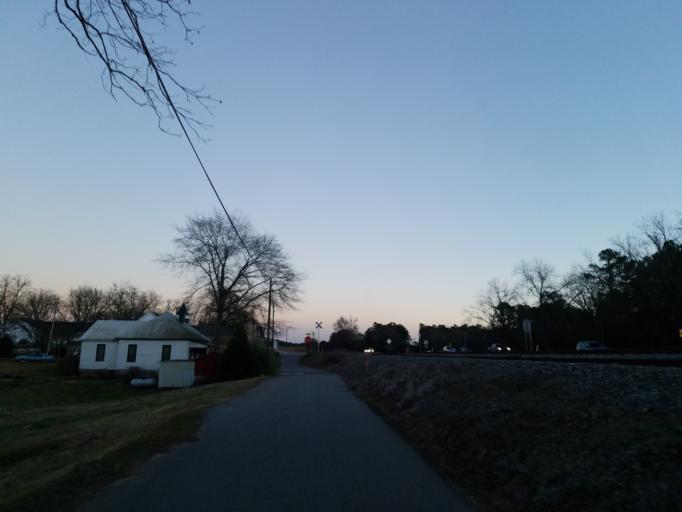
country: US
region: Georgia
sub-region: Monroe County
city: Forsyth
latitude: 32.9826
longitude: -83.8783
